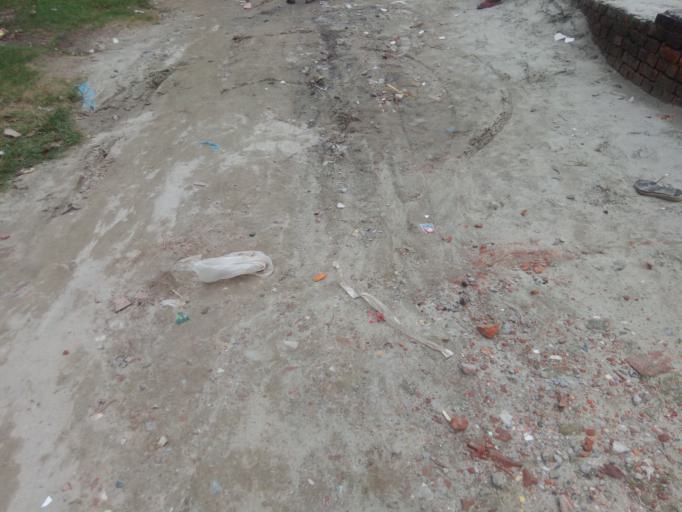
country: BD
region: Dhaka
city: Azimpur
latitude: 23.7417
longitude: 90.3561
